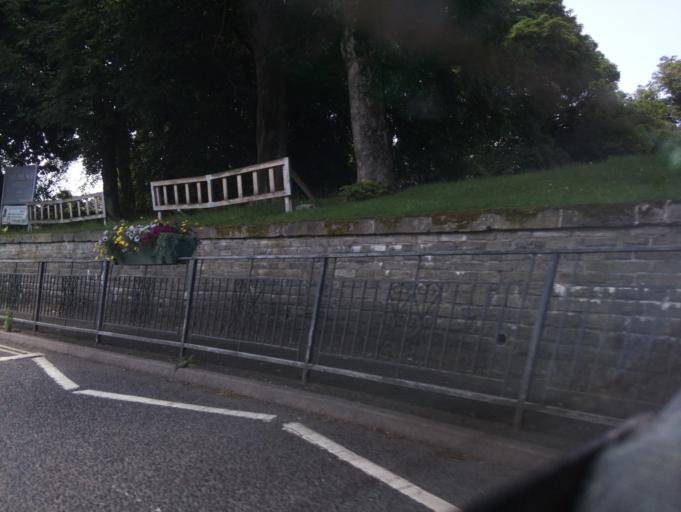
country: GB
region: England
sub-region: Derbyshire
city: Buxton
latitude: 53.2600
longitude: -1.9147
